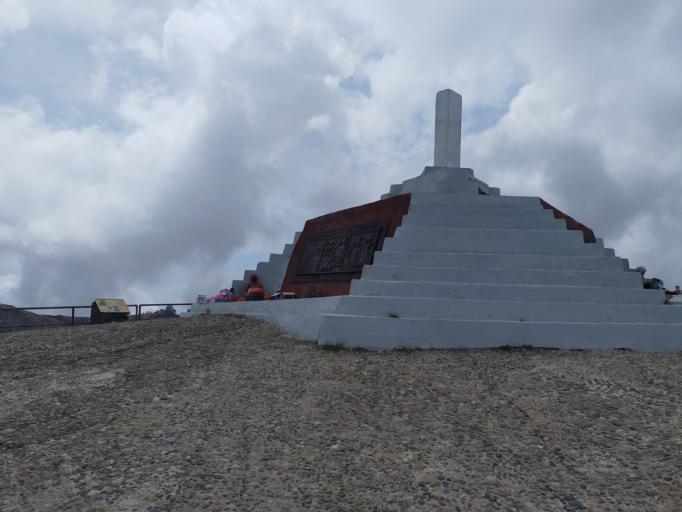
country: ID
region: East Nusa Tenggara
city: Koanara
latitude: -8.7642
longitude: 121.8123
